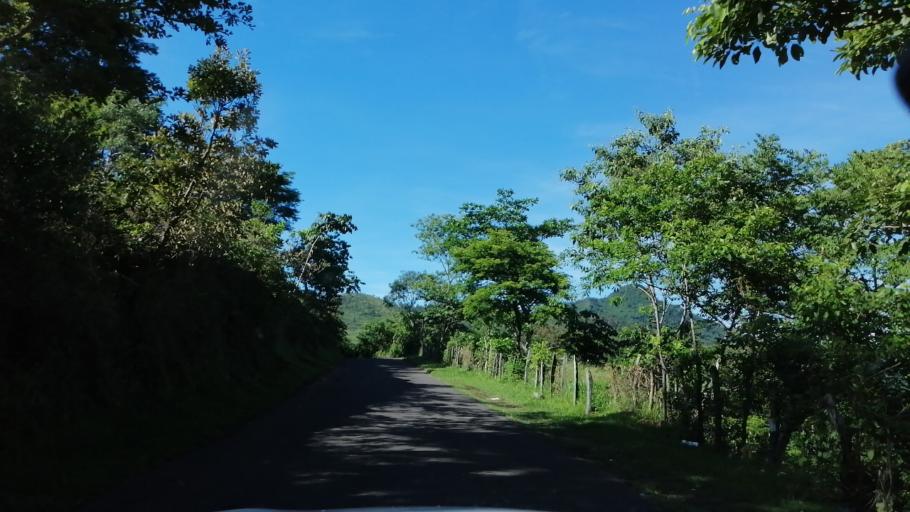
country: SV
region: Morazan
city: Corinto
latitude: 13.8112
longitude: -87.9802
